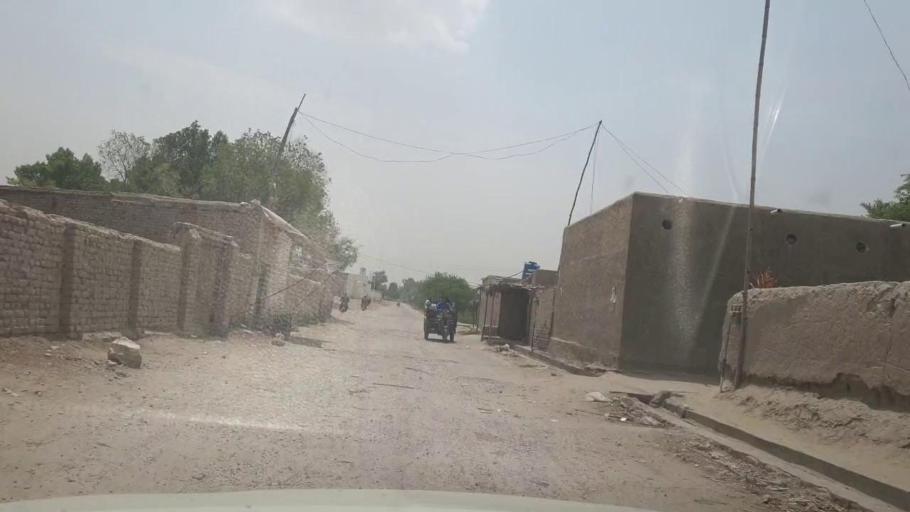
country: PK
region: Sindh
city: Kot Diji
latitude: 27.3699
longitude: 68.7223
